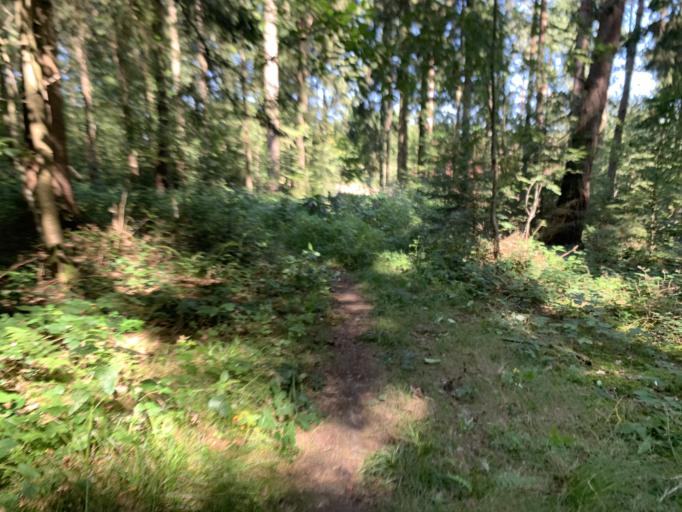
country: DE
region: Bavaria
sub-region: Upper Bavaria
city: Freising
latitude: 48.4219
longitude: 11.7487
